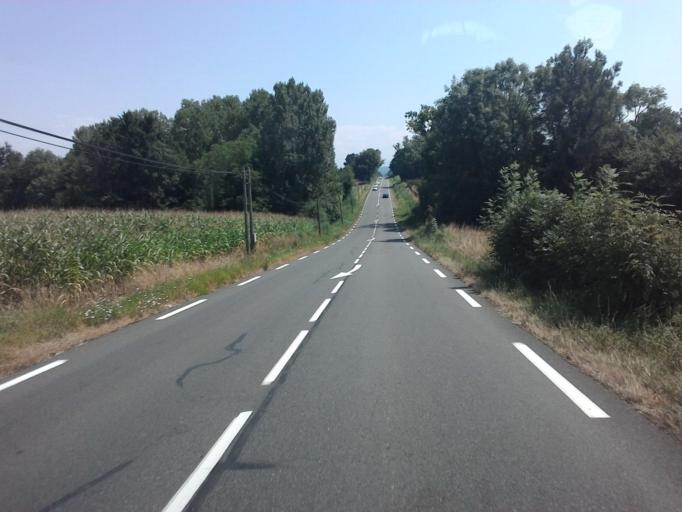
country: FR
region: Rhone-Alpes
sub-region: Departement de l'Isere
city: Fitilieu
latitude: 45.5630
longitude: 5.5647
